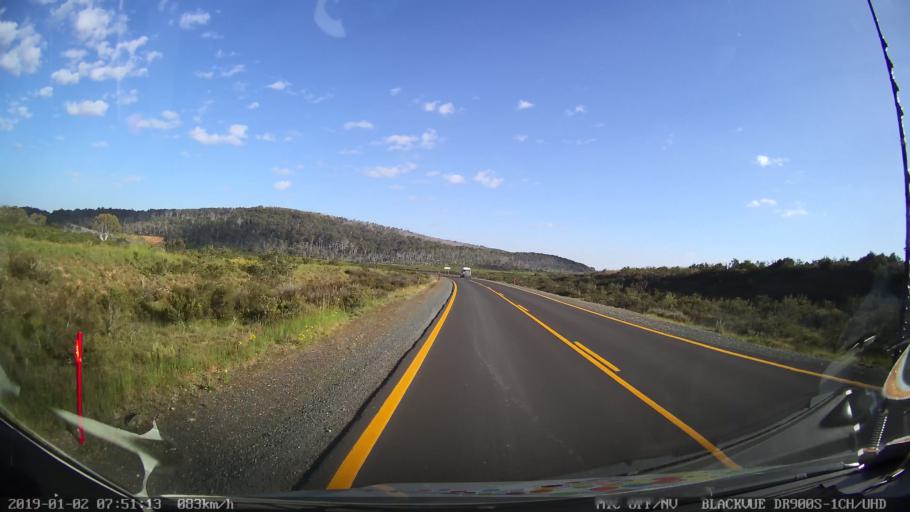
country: AU
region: New South Wales
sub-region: Tumut Shire
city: Tumut
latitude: -35.7209
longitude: 148.5311
